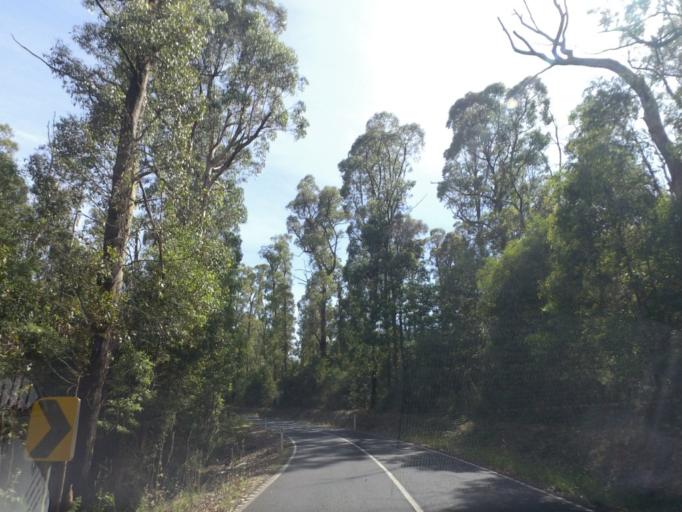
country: AU
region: Victoria
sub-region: Nillumbik
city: Saint Andrews
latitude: -37.5416
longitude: 145.3388
